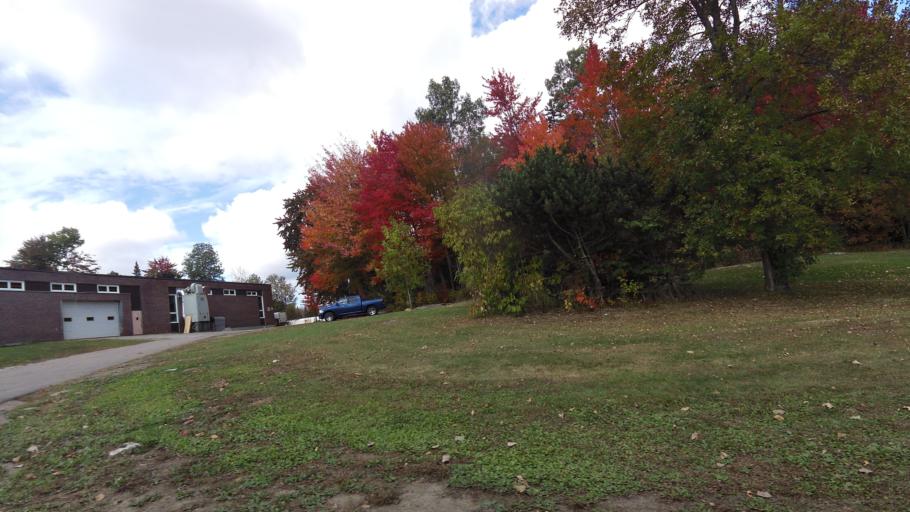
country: CA
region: Ontario
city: Deep River
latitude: 46.1051
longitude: -77.4880
